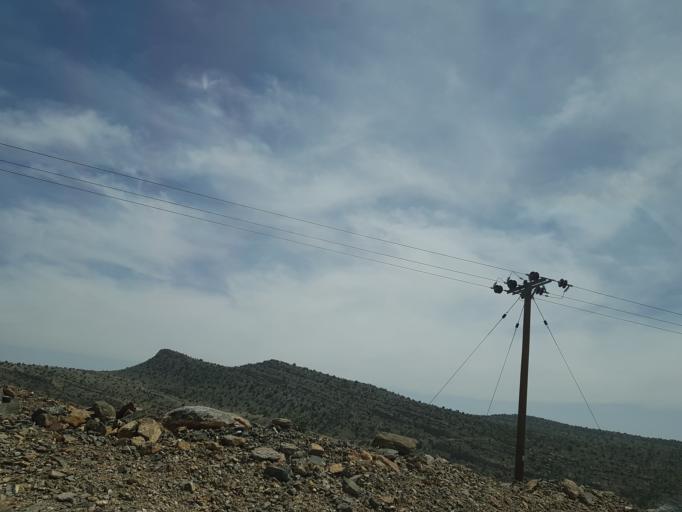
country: OM
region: Al Batinah
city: Bayt al `Awabi
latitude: 23.1348
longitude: 57.5686
